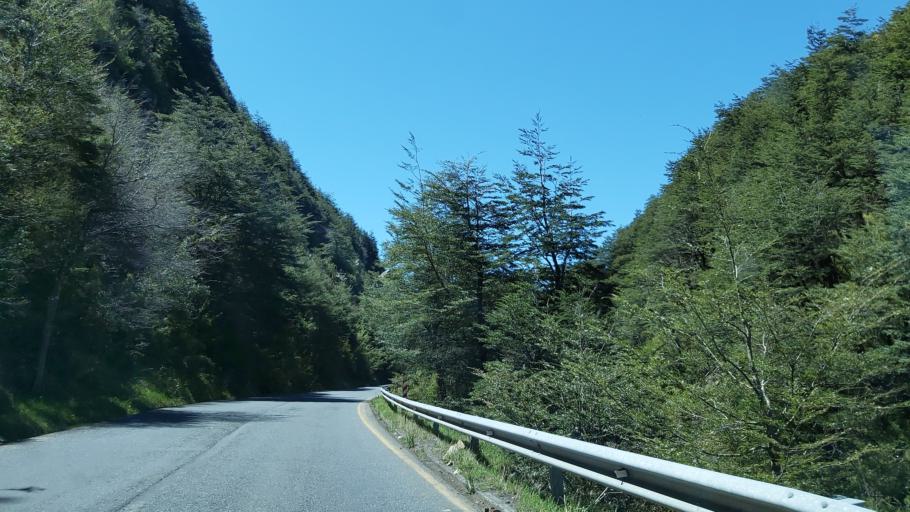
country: CL
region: Araucania
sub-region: Provincia de Cautin
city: Vilcun
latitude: -38.4696
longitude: -71.6442
